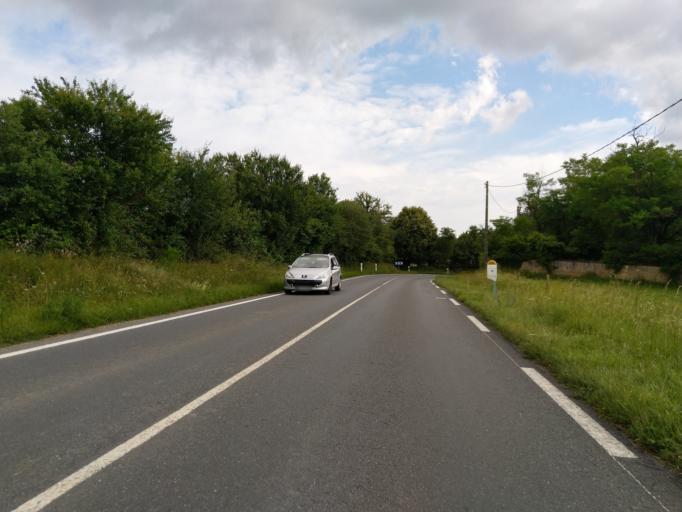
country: FR
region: Midi-Pyrenees
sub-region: Departement du Tarn
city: Realmont
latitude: 43.8086
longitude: 2.1600
